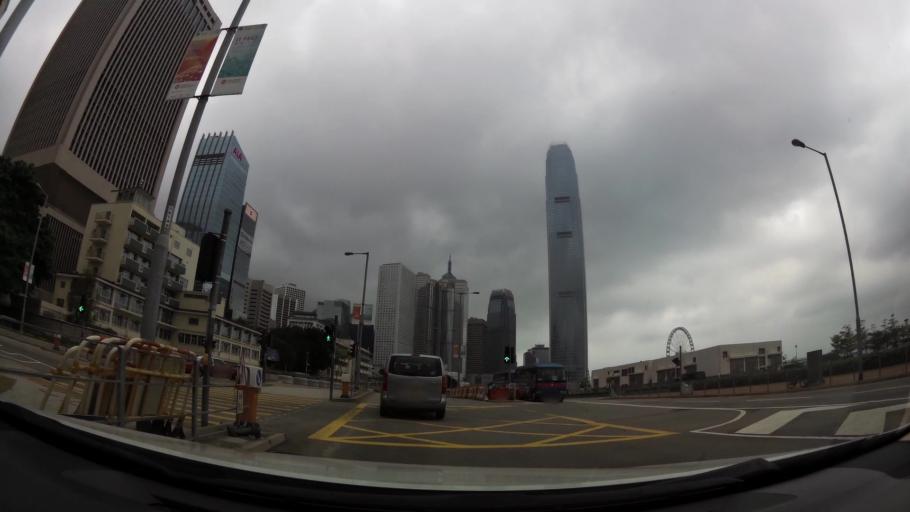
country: HK
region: Central and Western
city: Central
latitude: 22.2824
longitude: 114.1650
